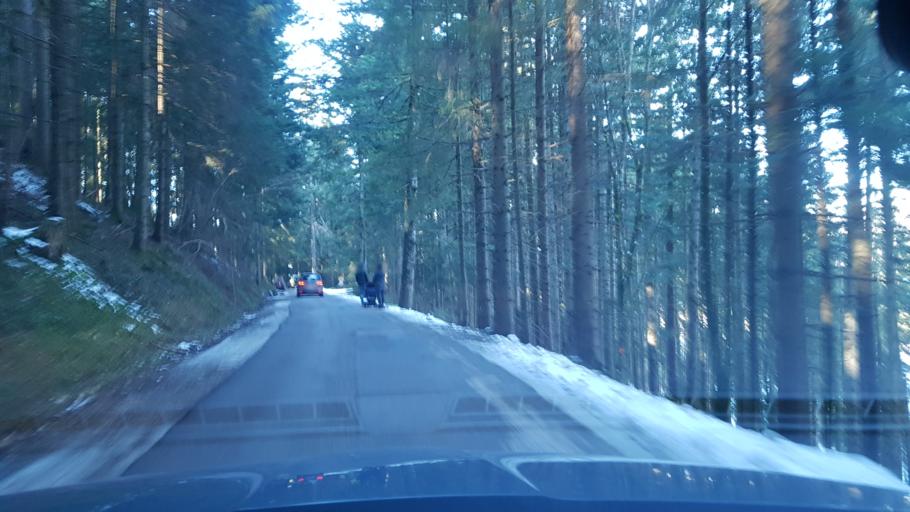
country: AT
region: Salzburg
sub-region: Politischer Bezirk Hallein
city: Scheffau am Tennengebirge
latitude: 47.6331
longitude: 13.2077
